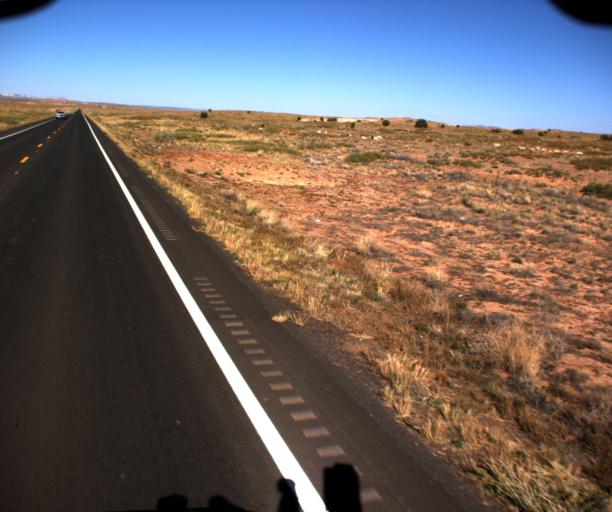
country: US
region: Arizona
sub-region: Coconino County
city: Tuba City
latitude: 36.2468
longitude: -111.0232
